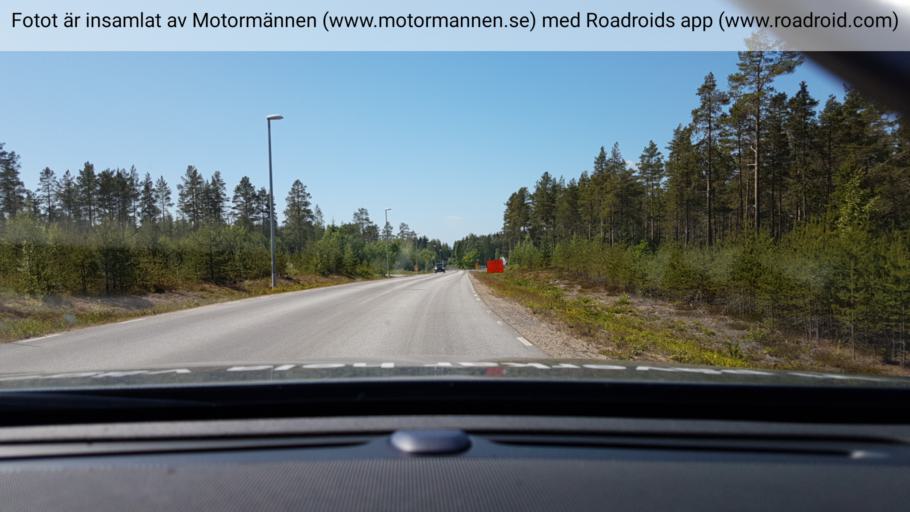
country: SE
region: Vaesterbotten
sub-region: Nordmalings Kommun
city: Nordmaling
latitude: 63.5807
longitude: 19.5336
